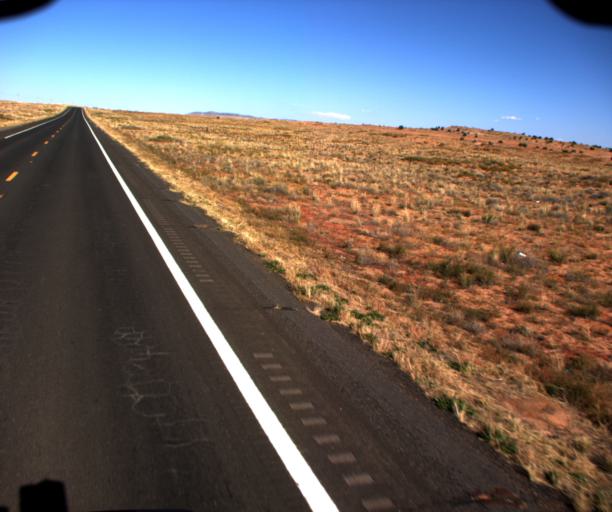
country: US
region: Arizona
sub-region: Coconino County
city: Tuba City
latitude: 36.2872
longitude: -110.9957
